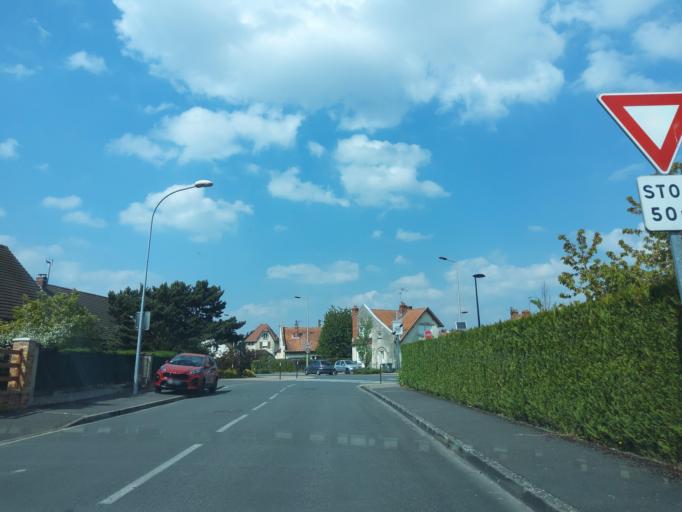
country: FR
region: Picardie
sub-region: Departement de l'Aisne
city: Laon
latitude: 49.5755
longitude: 3.6332
